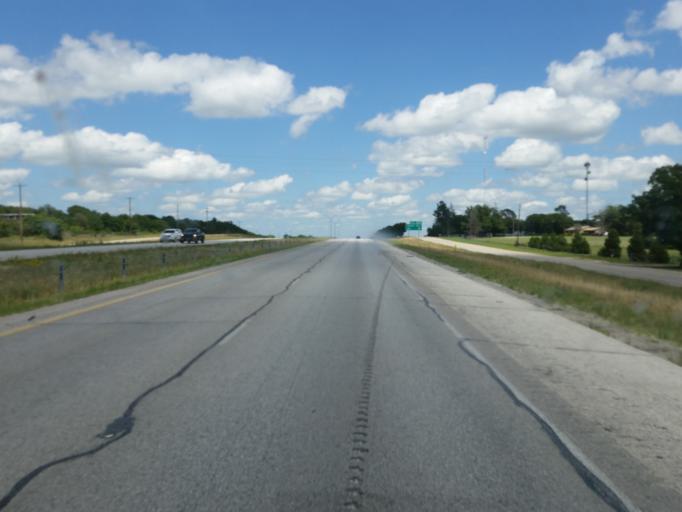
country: US
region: Texas
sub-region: Callahan County
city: Clyde
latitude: 32.4087
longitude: -99.4641
